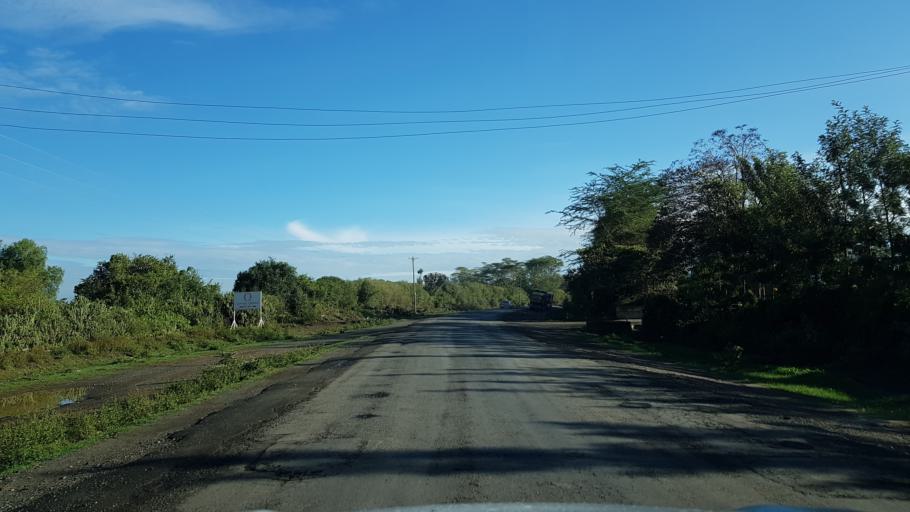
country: KE
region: Nakuru
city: Naivasha
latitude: -0.7828
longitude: 36.4255
